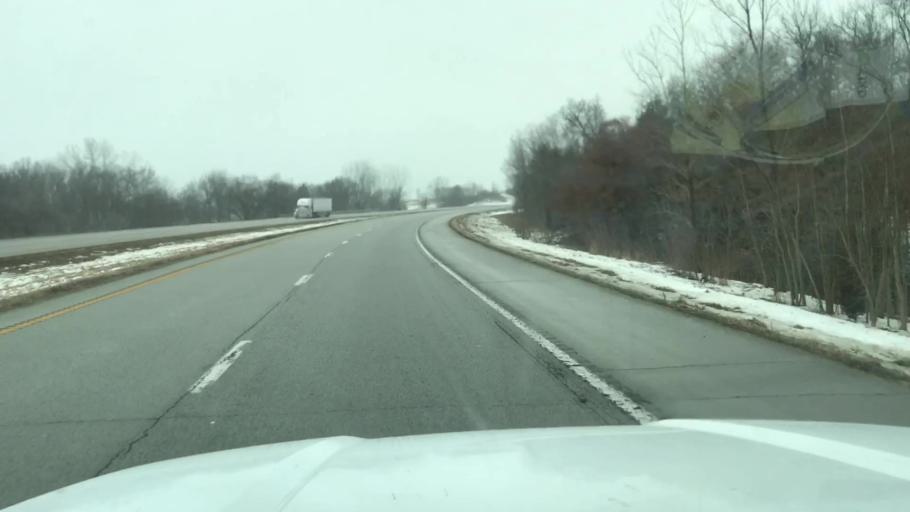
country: US
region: Missouri
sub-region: Clinton County
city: Gower
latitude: 39.7479
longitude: -94.6044
